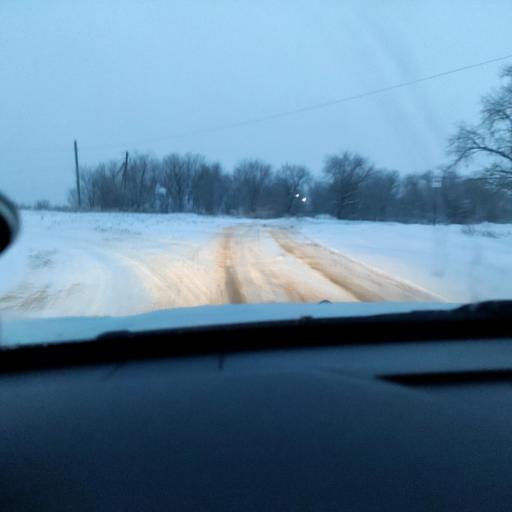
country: RU
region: Samara
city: Smyshlyayevka
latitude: 53.2409
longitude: 50.4801
